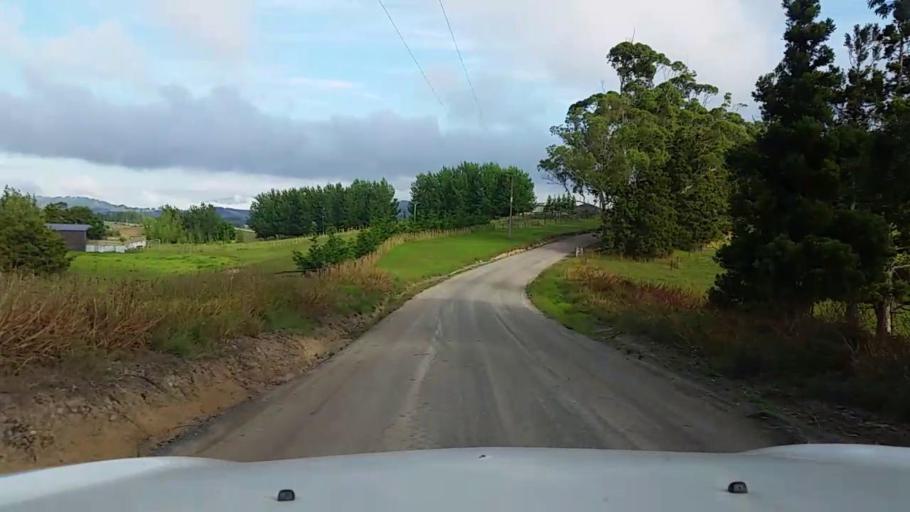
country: NZ
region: Northland
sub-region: Whangarei
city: Maungatapere
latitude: -35.6733
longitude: 174.1759
